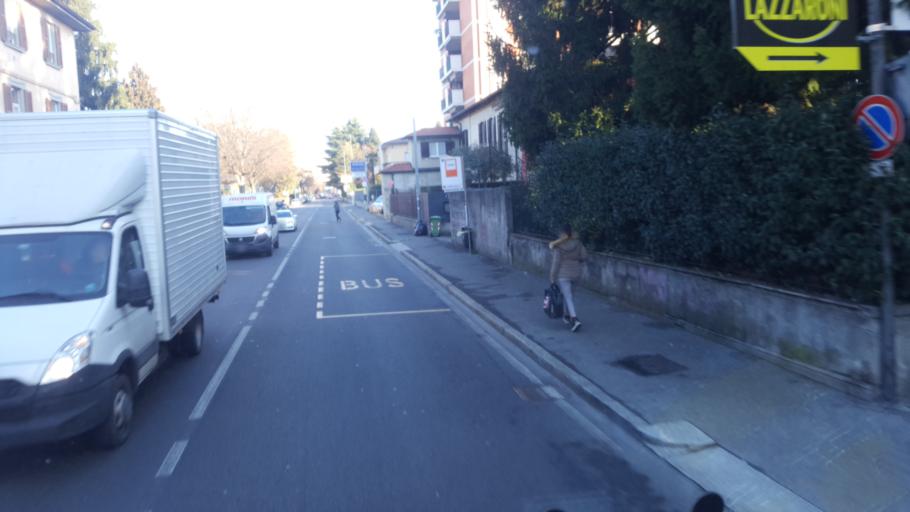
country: IT
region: Lombardy
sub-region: Provincia di Bergamo
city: Bergamo
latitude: 45.6795
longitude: 9.6617
